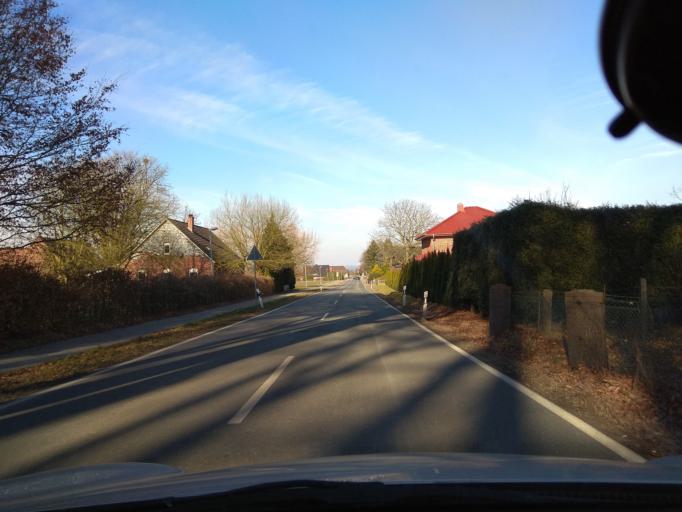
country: DE
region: North Rhine-Westphalia
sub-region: Regierungsbezirk Munster
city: Mettingen
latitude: 52.3010
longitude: 7.7765
